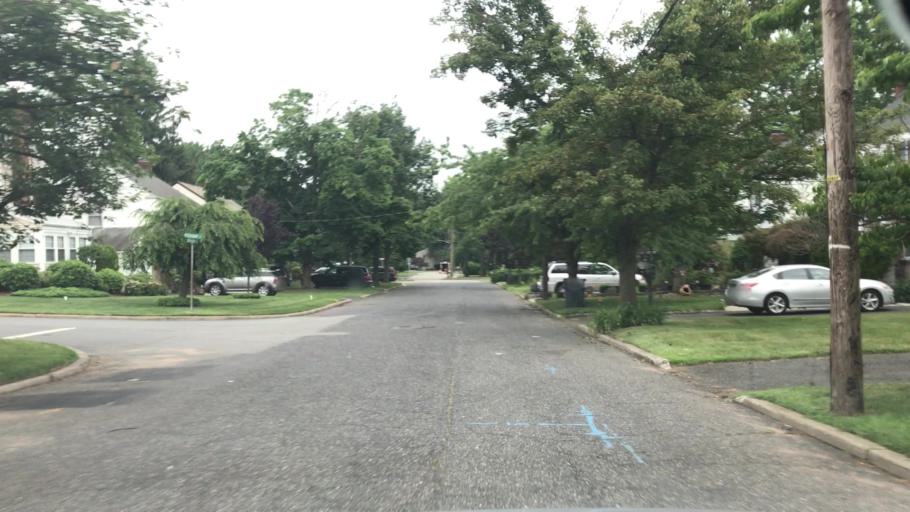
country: US
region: New Jersey
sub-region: Bergen County
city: Bergenfield
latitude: 40.9221
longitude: -73.9917
